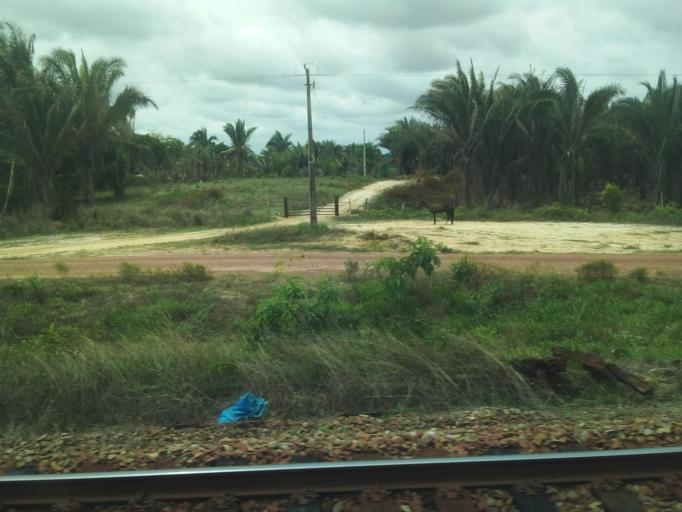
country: BR
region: Maranhao
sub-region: Santa Ines
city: Santa Ines
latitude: -3.6539
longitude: -45.8202
